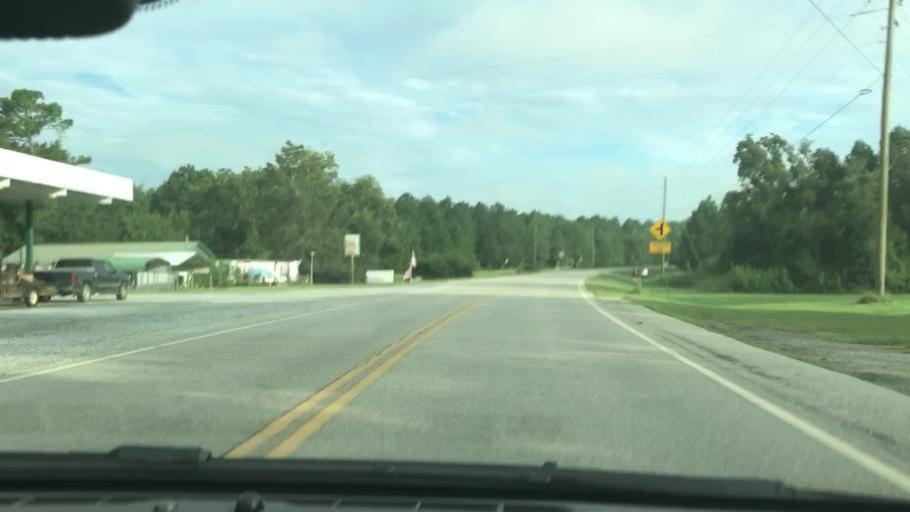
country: US
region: Georgia
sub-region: Quitman County
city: Georgetown
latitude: 31.7695
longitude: -85.0910
